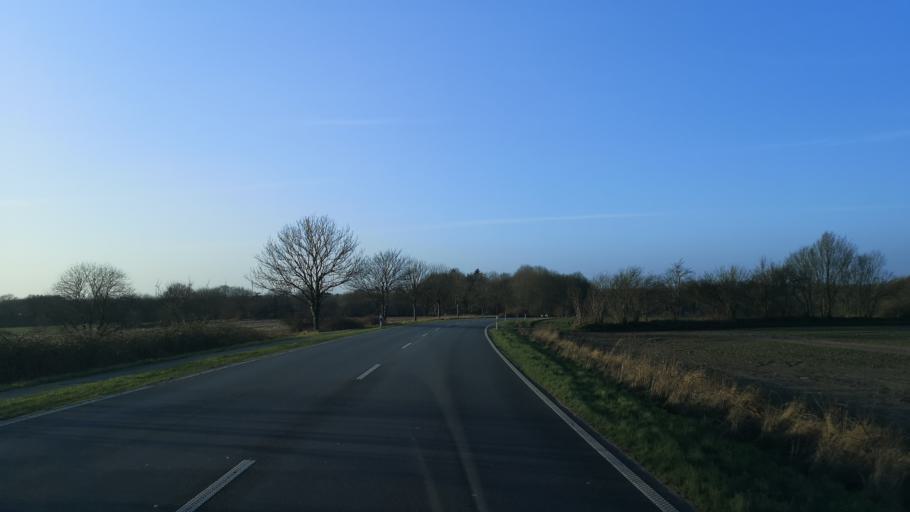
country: DE
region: Schleswig-Holstein
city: Tarp
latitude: 54.6645
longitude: 9.4193
